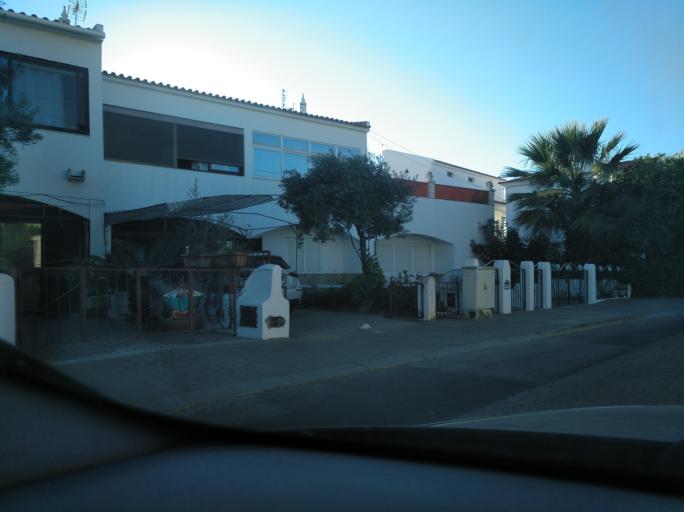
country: PT
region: Faro
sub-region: Vila Real de Santo Antonio
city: Monte Gordo
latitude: 37.1717
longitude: -7.5187
